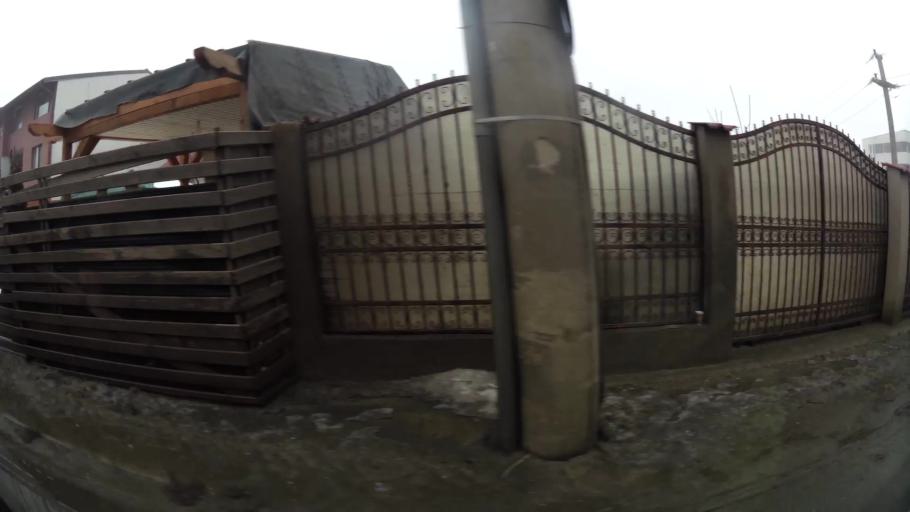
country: RO
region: Ilfov
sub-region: Comuna Chiajna
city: Chiajna
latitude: 44.4497
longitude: 25.9841
